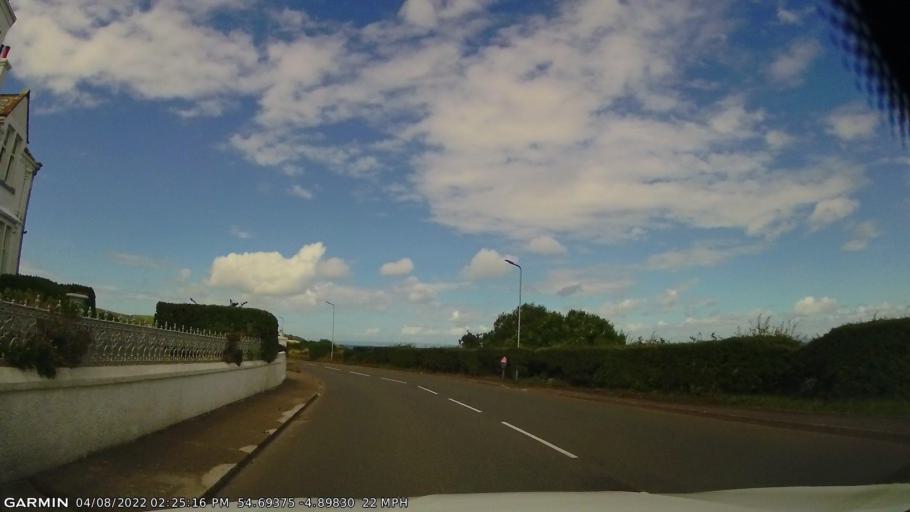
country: GB
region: Scotland
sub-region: Dumfries and Galloway
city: Stranraer
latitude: 54.6937
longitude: -4.8983
